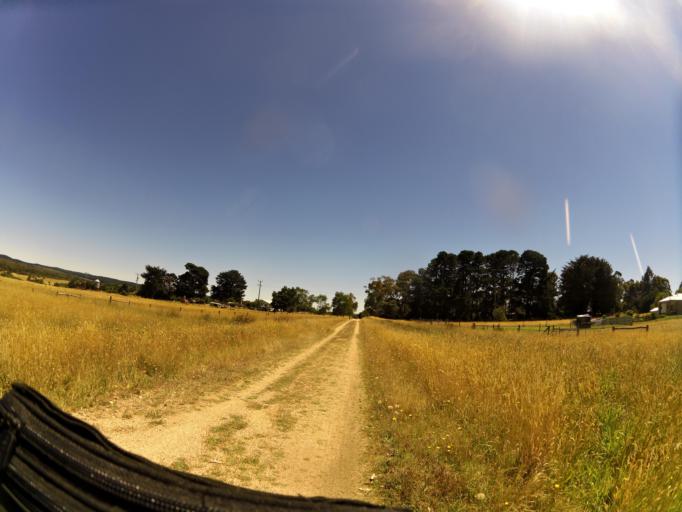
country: AU
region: Victoria
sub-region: Ballarat North
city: Delacombe
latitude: -37.6918
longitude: 143.6545
